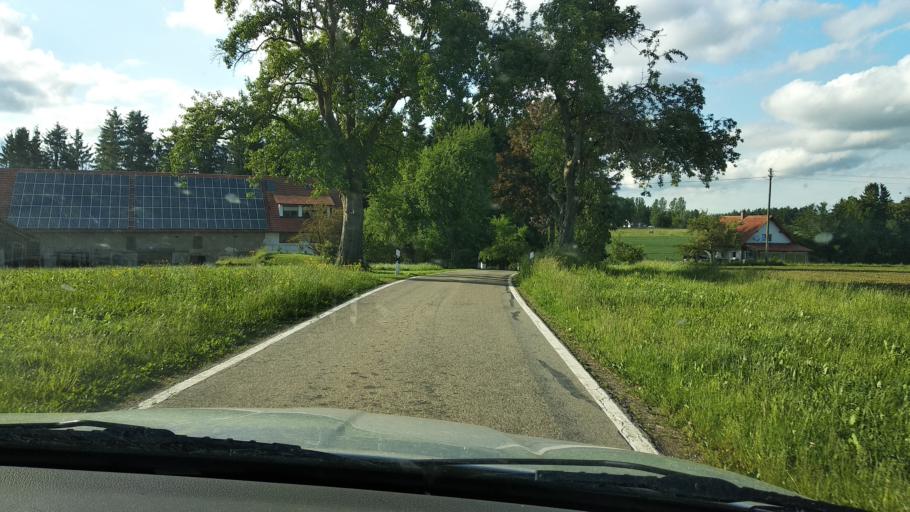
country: DE
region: Baden-Wuerttemberg
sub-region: Tuebingen Region
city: Aitrach
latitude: 47.9457
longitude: 10.0433
